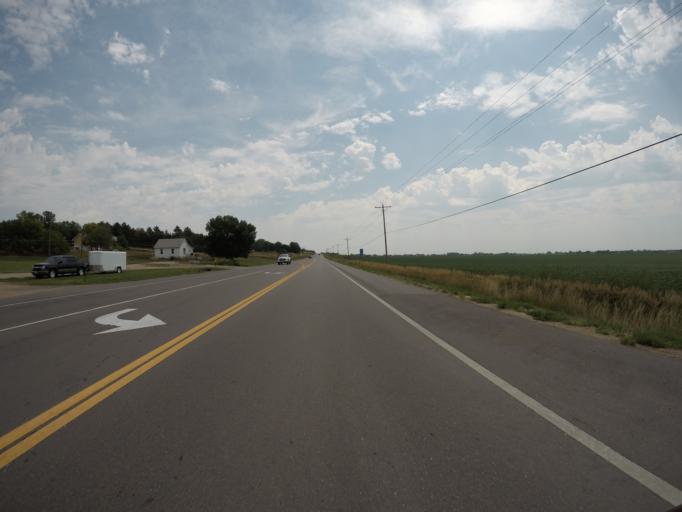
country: US
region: Nebraska
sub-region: Buffalo County
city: Kearney
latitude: 40.6994
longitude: -99.1609
